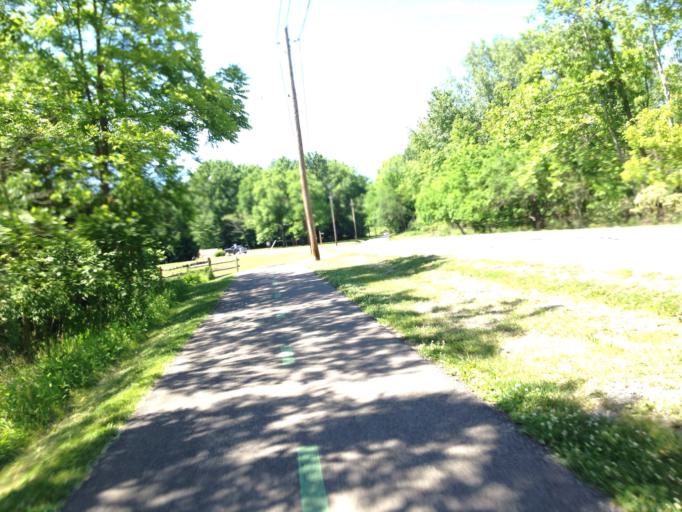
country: US
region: Ohio
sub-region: Cuyahoga County
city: Berea
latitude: 41.3504
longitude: -81.8437
